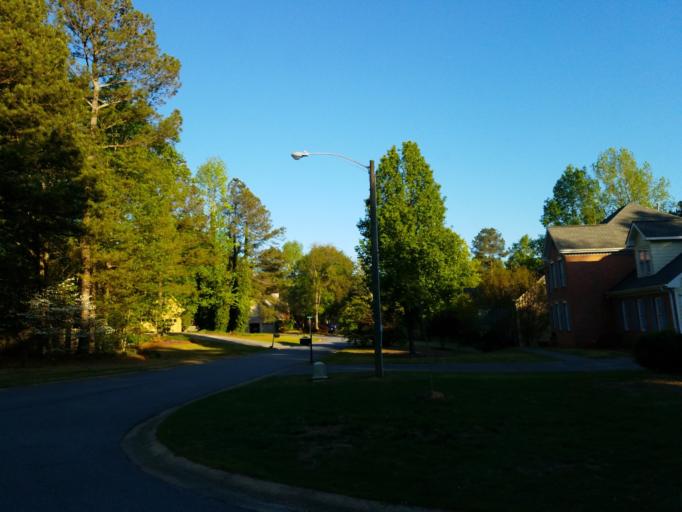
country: US
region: Georgia
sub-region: Cobb County
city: Powder Springs
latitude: 33.9210
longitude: -84.6397
